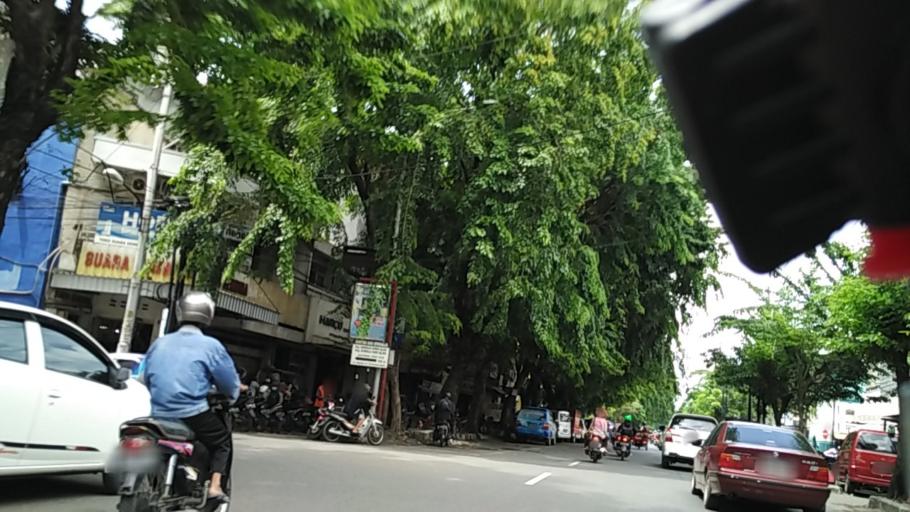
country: ID
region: Central Java
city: Semarang
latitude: -6.9785
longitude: 110.4313
